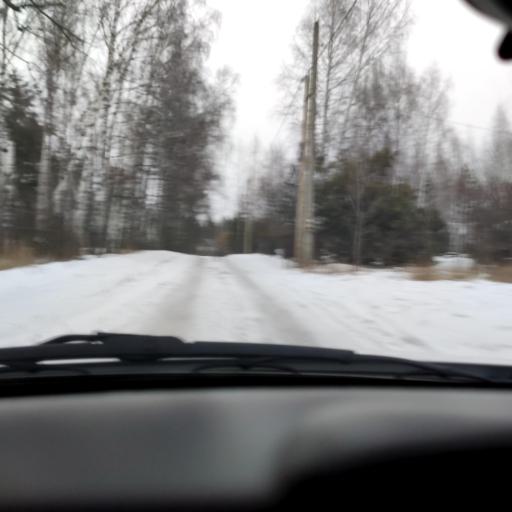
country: RU
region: Voronezj
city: Ramon'
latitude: 51.8805
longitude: 39.2657
